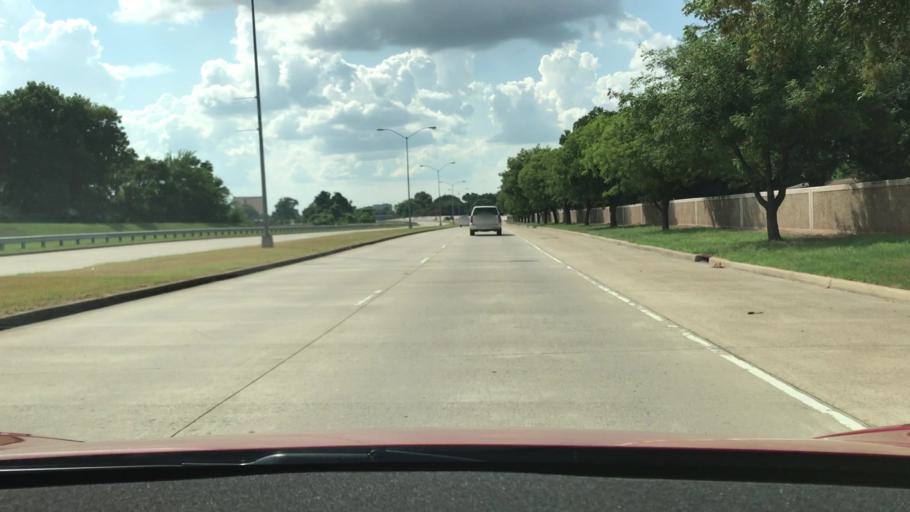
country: US
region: Louisiana
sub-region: Bossier Parish
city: Bossier City
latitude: 32.5075
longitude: -93.7135
